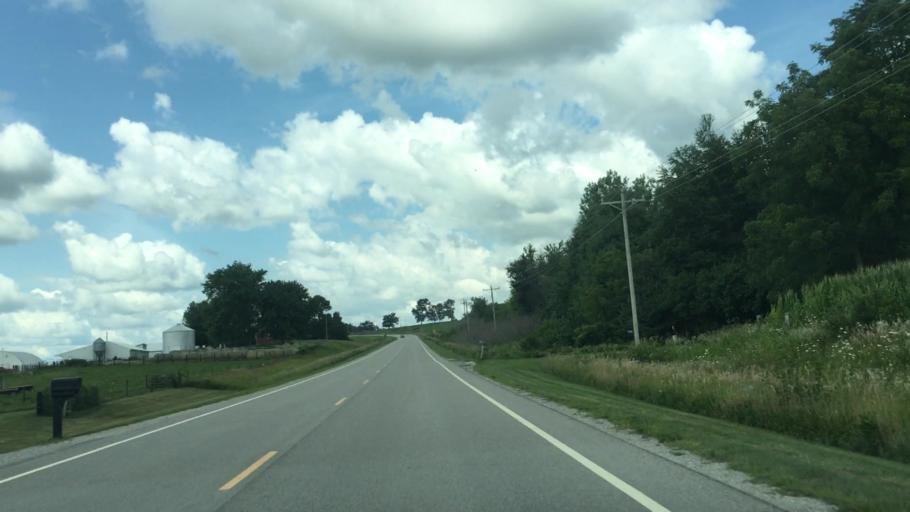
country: US
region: Iowa
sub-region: Linn County
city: Mount Vernon
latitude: 41.8421
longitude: -91.4116
